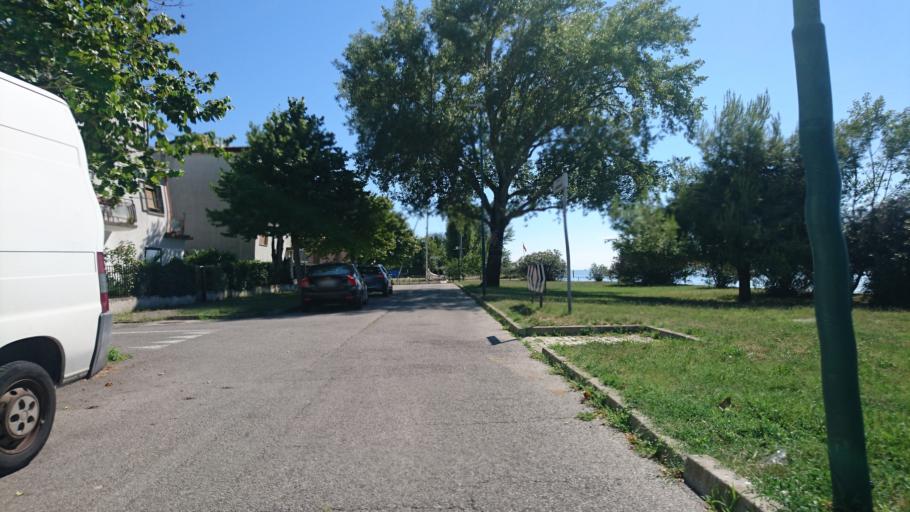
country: IT
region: Veneto
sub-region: Provincia di Venezia
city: Lido
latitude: 45.3888
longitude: 12.3487
